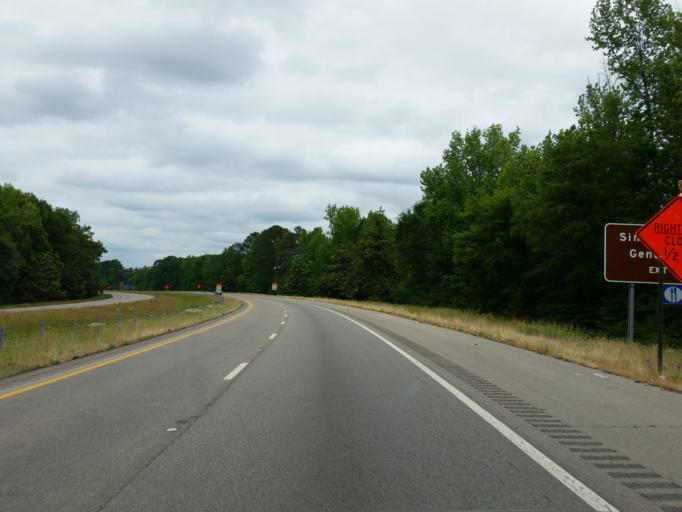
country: US
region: Alabama
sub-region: Sumter County
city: York
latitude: 32.4133
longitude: -88.4623
